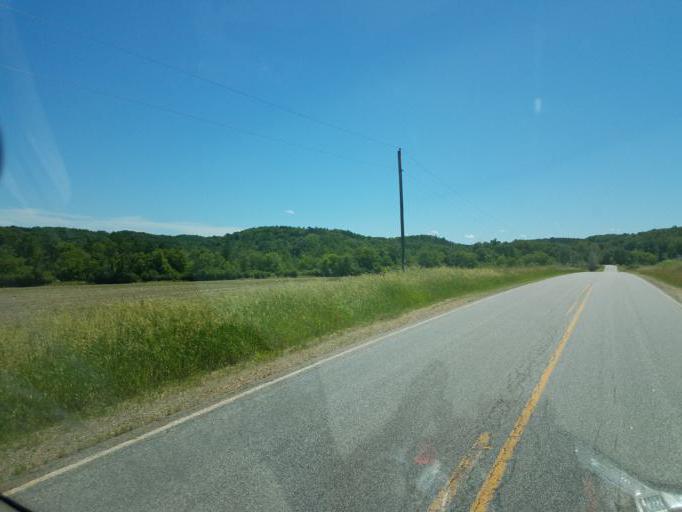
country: US
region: Wisconsin
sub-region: Juneau County
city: Elroy
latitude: 43.8567
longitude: -90.2864
